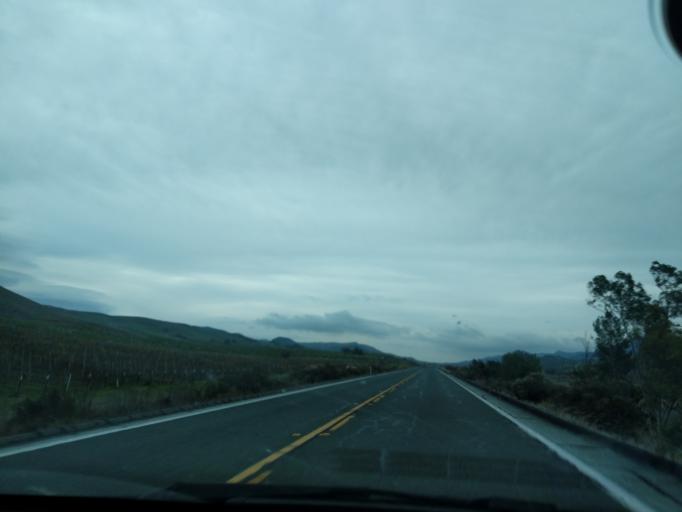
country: US
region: California
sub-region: San Benito County
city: Ridgemark
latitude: 36.6999
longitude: -121.2738
